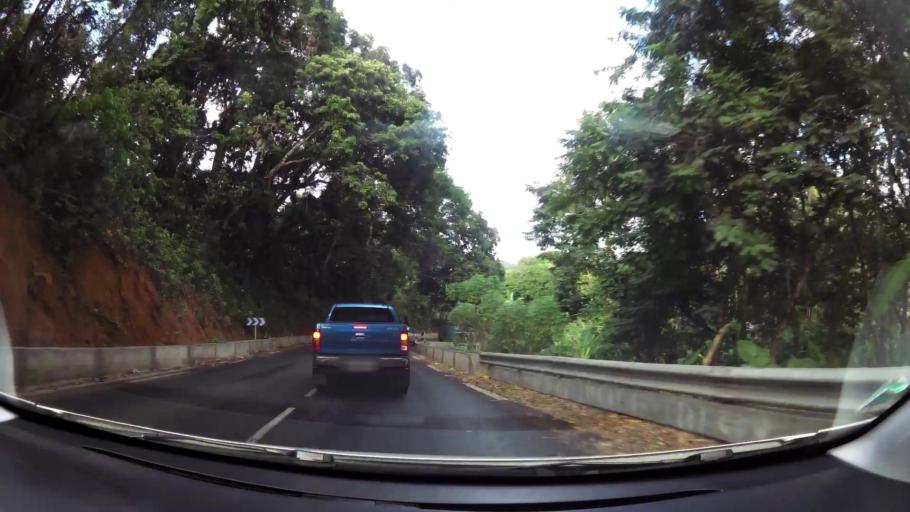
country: YT
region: Ouangani
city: Ouangani
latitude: -12.8368
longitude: 45.1513
